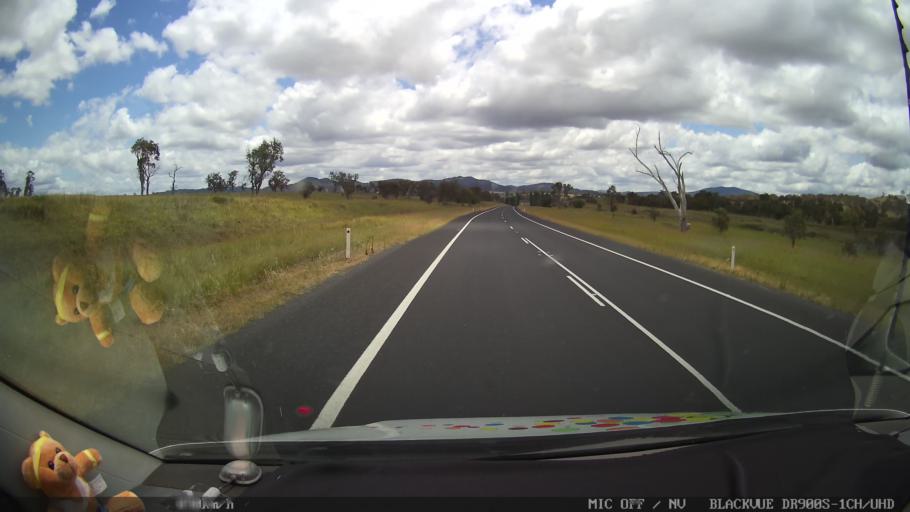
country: AU
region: New South Wales
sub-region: Glen Innes Severn
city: Glen Innes
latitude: -29.3929
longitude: 151.8815
